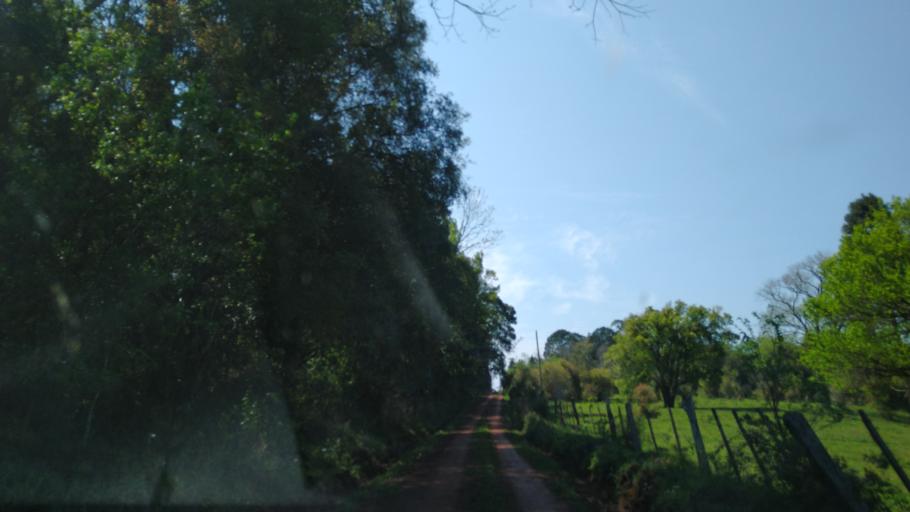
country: AR
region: Misiones
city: Capiovi
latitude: -26.9439
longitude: -55.0454
